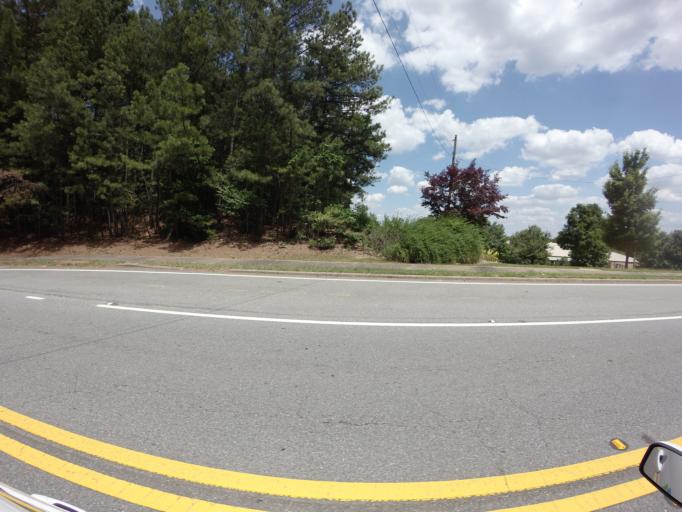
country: US
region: Georgia
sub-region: Fulton County
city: Johns Creek
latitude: 34.0113
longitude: -84.2519
